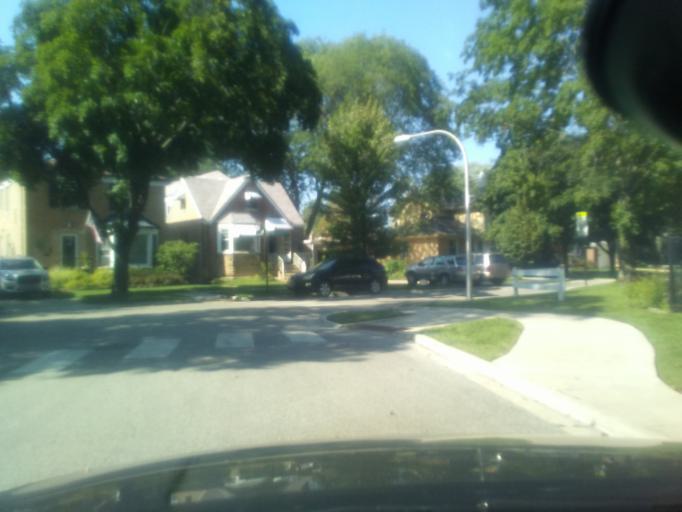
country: US
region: Illinois
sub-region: Cook County
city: Lincolnwood
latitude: 41.9845
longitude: -87.7420
